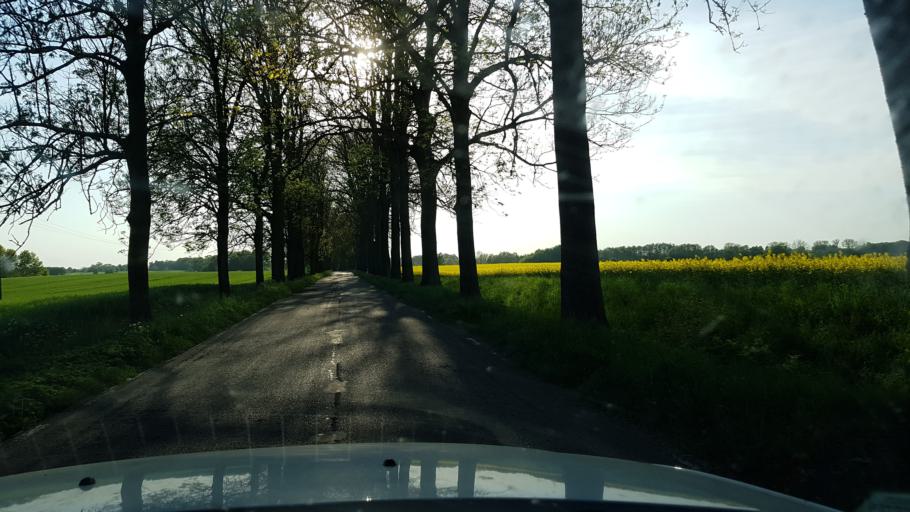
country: PL
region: West Pomeranian Voivodeship
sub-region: Powiat lobeski
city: Dobra
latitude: 53.5758
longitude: 15.2604
